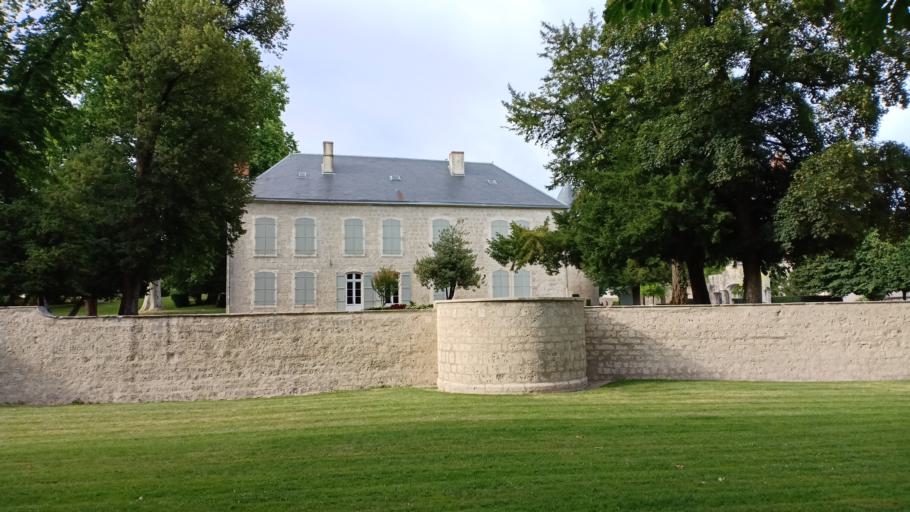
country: FR
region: Poitou-Charentes
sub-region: Departement de la Charente-Maritime
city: Surgeres
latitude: 46.1044
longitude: -0.7516
